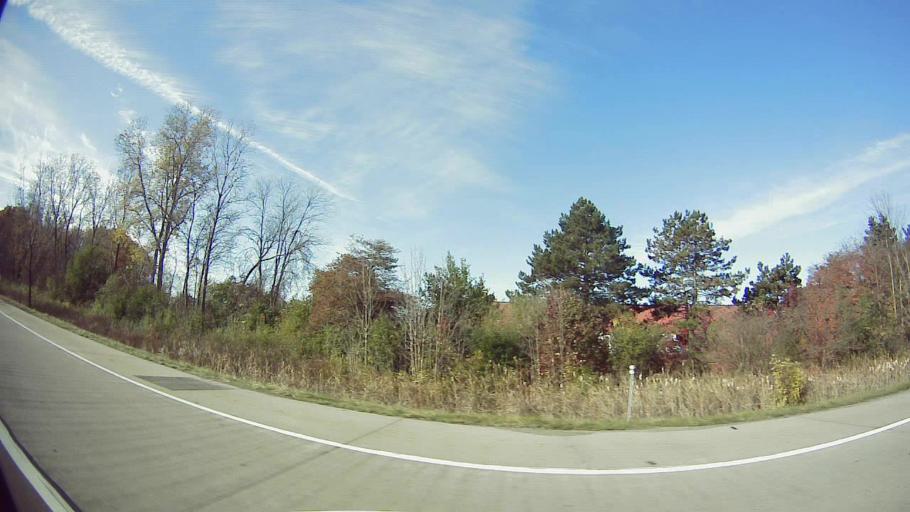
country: US
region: Michigan
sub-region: Wayne County
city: Westland
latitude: 42.3303
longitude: -83.4438
